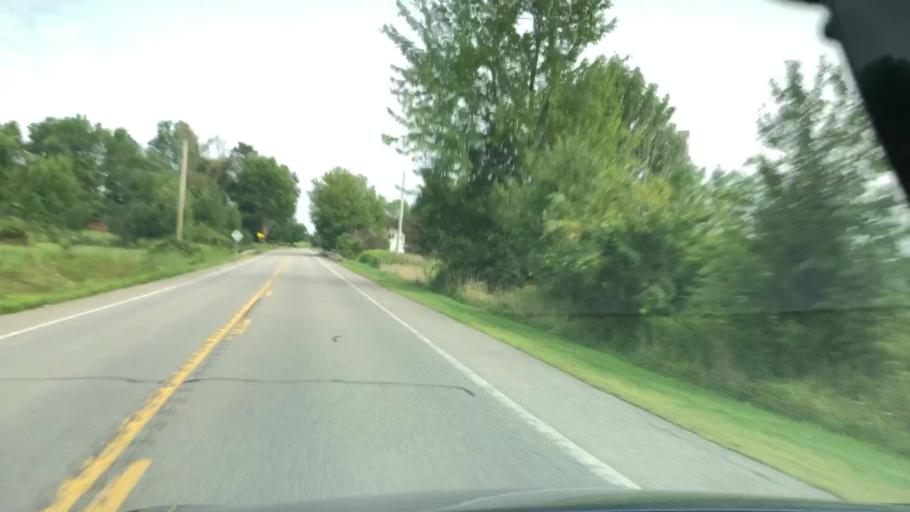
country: US
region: Pennsylvania
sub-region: Erie County
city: Union City
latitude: 41.8177
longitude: -79.8066
